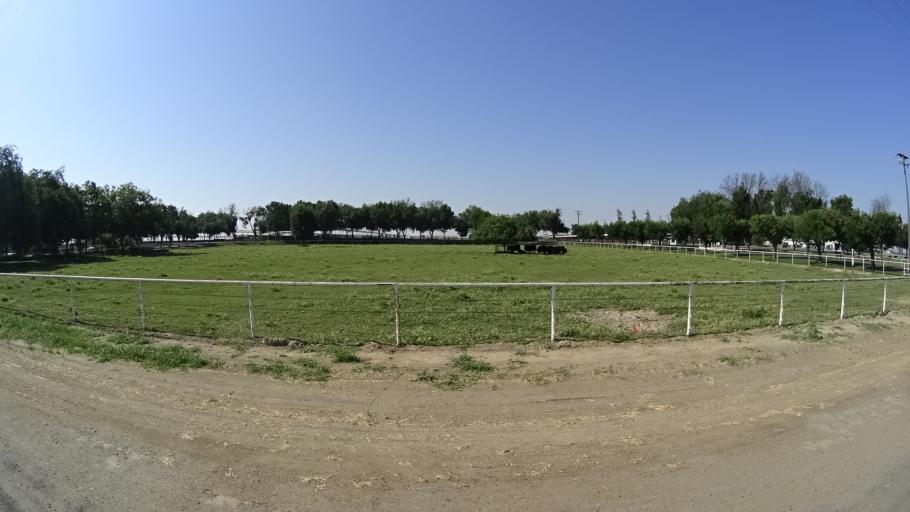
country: US
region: California
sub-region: Fresno County
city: Kingsburg
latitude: 36.4160
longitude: -119.5339
